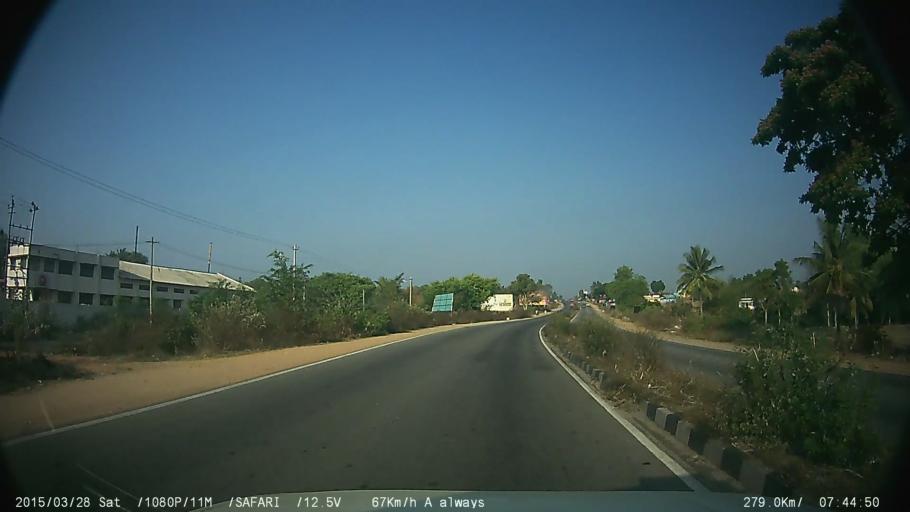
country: IN
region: Karnataka
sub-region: Mandya
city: Mandya
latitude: 12.4954
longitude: 76.8003
